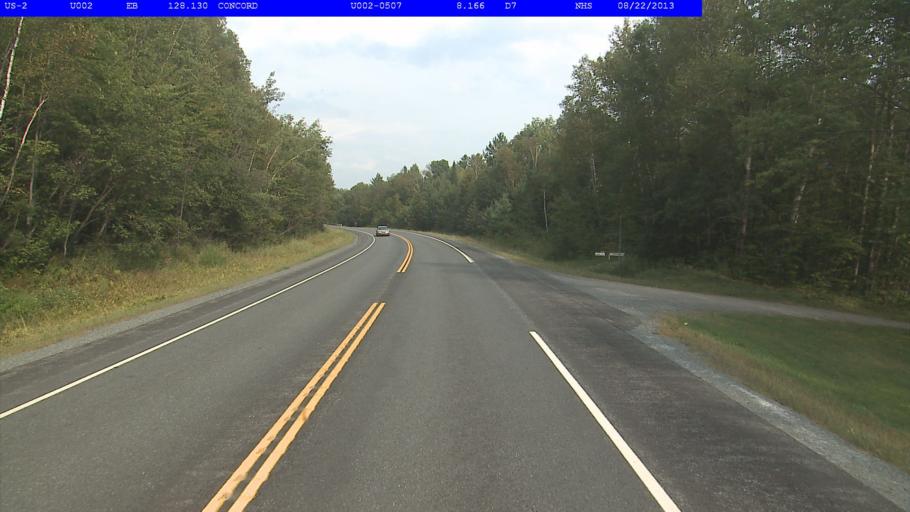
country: US
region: New Hampshire
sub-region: Grafton County
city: Littleton
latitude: 44.4513
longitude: -71.8129
